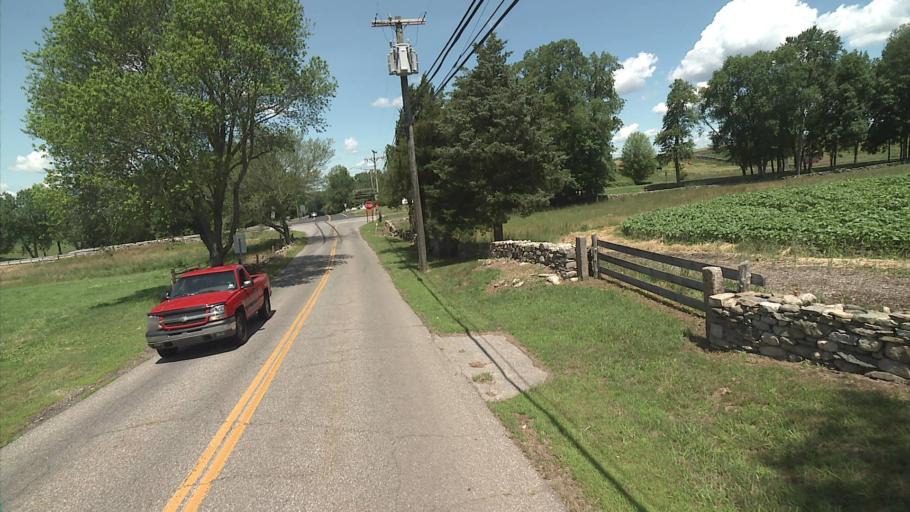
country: US
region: Connecticut
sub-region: New London County
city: Preston City
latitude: 41.5520
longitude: -71.8849
